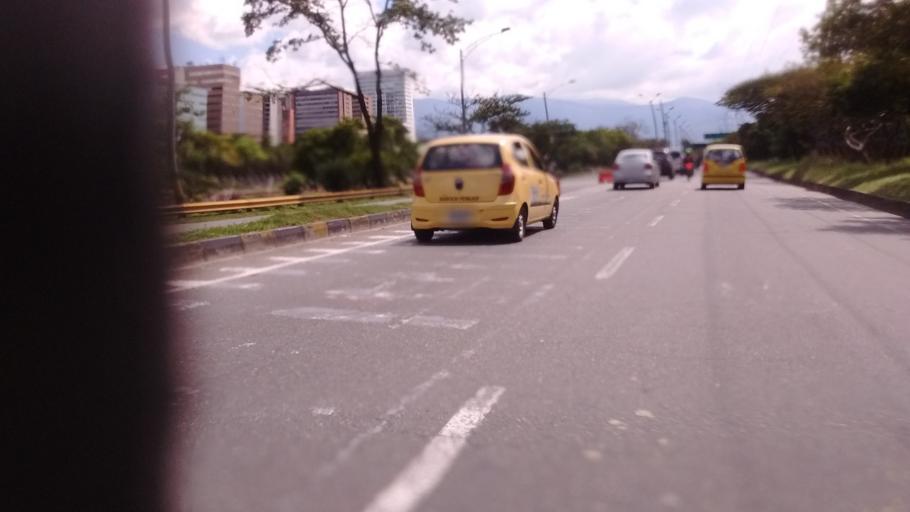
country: CO
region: Antioquia
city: Medellin
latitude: 6.2282
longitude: -75.5764
